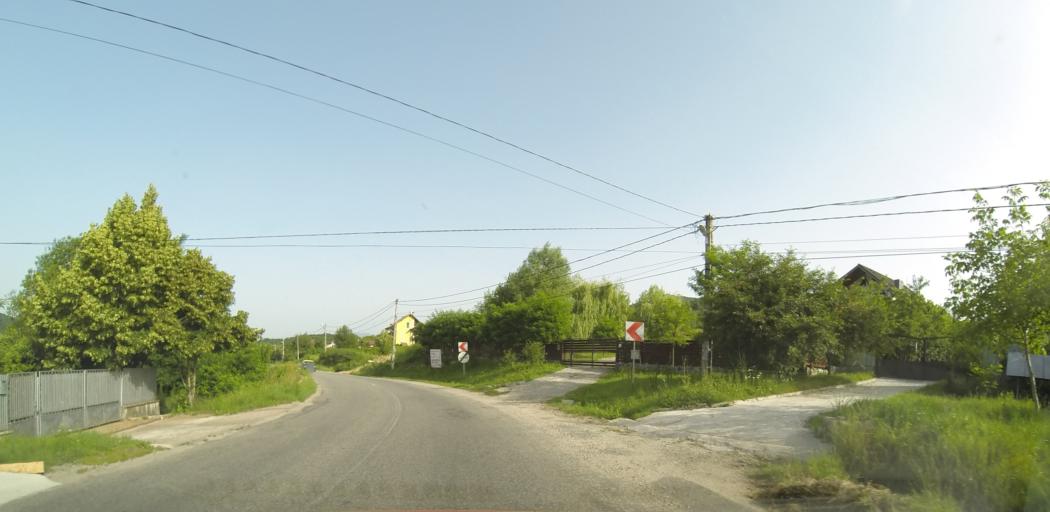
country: RO
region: Valcea
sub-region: Comuna Vladesti
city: Vladesti
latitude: 45.1244
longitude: 24.2871
